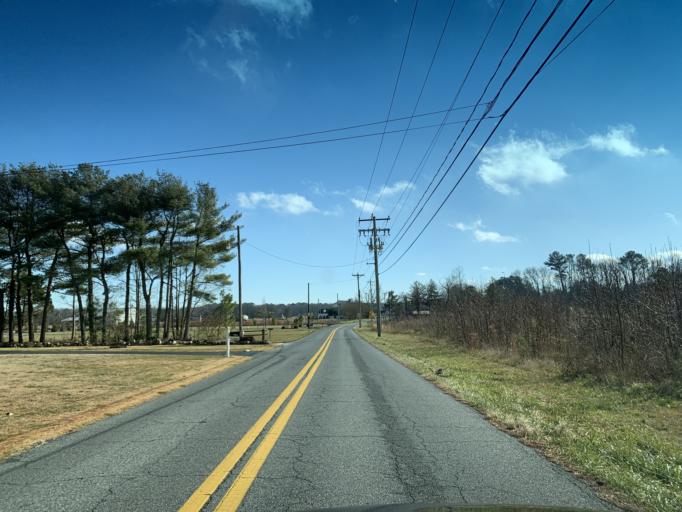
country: US
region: Delaware
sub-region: Sussex County
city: Selbyville
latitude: 38.4521
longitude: -75.1966
